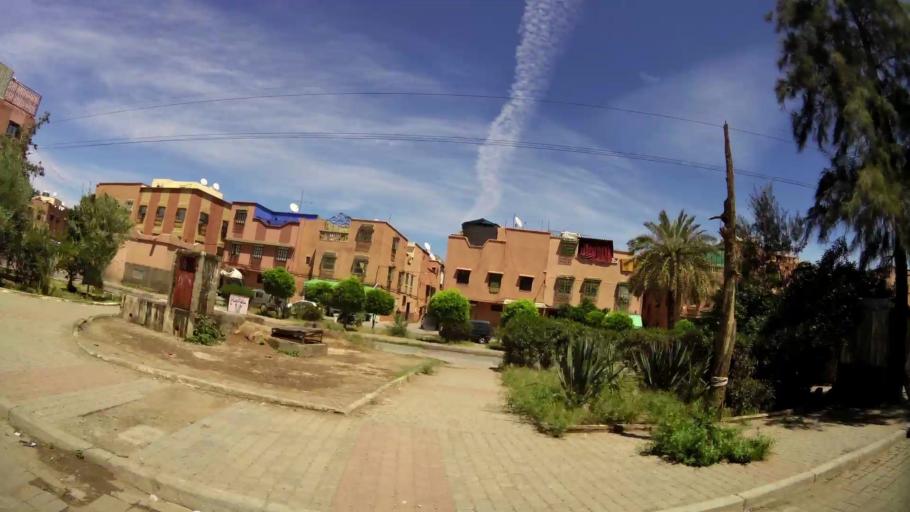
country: MA
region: Marrakech-Tensift-Al Haouz
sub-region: Marrakech
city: Marrakesh
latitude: 31.6362
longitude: -8.0440
